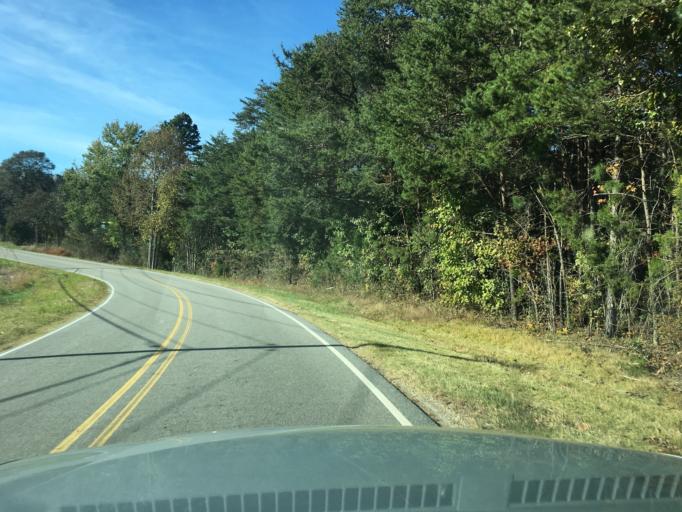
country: US
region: North Carolina
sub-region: Catawba County
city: Saint Stephens
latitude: 35.7106
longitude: -81.2774
